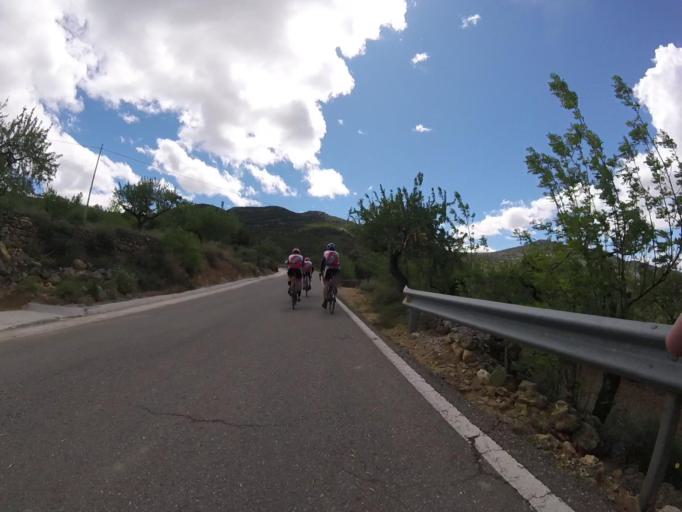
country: ES
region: Valencia
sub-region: Provincia de Castello
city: Sierra-Engarceran
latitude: 40.2936
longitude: -0.0412
